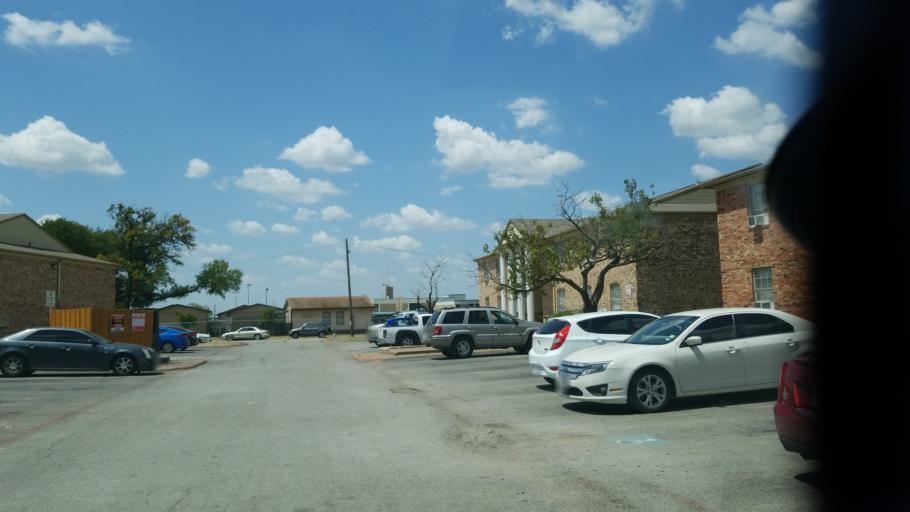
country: US
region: Texas
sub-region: Dallas County
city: Cockrell Hill
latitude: 32.7352
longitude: -96.9232
